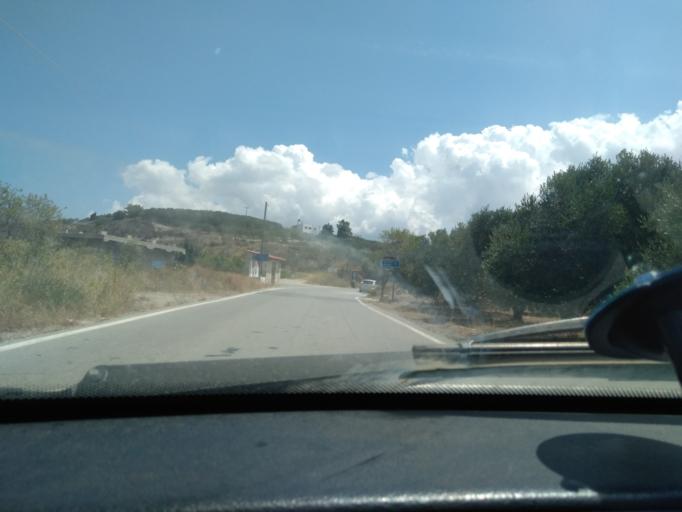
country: GR
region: Crete
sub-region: Nomos Lasithiou
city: Siteia
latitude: 35.1014
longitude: 26.0707
